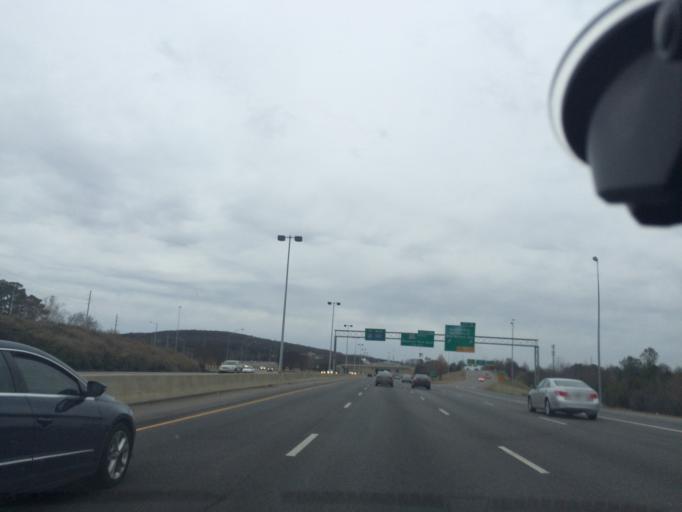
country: US
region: Alabama
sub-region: Madison County
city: Redstone Arsenal
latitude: 34.7172
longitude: -86.6382
